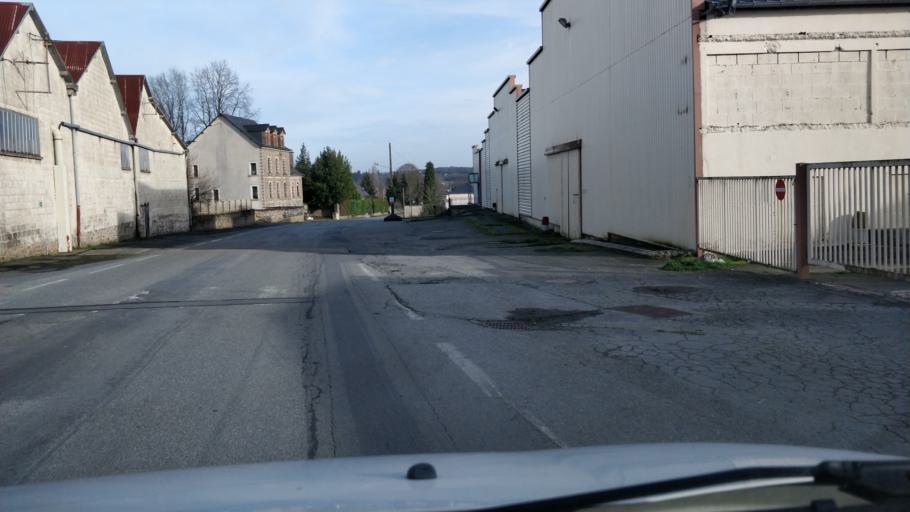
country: FR
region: Brittany
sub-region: Departement d'Ille-et-Vilaine
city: Argentre-du-Plessis
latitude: 48.0519
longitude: -1.1612
